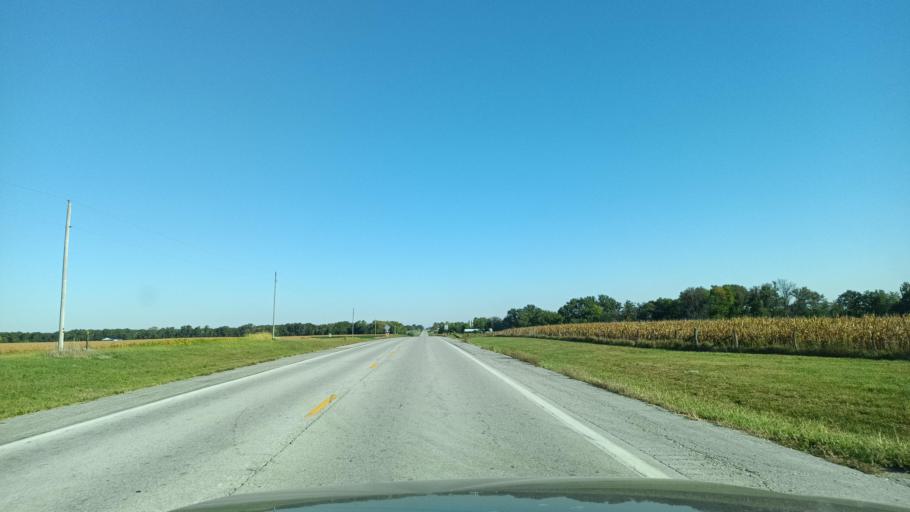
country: US
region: Missouri
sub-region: Audrain County
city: Vandalia
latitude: 39.2956
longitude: -91.6439
